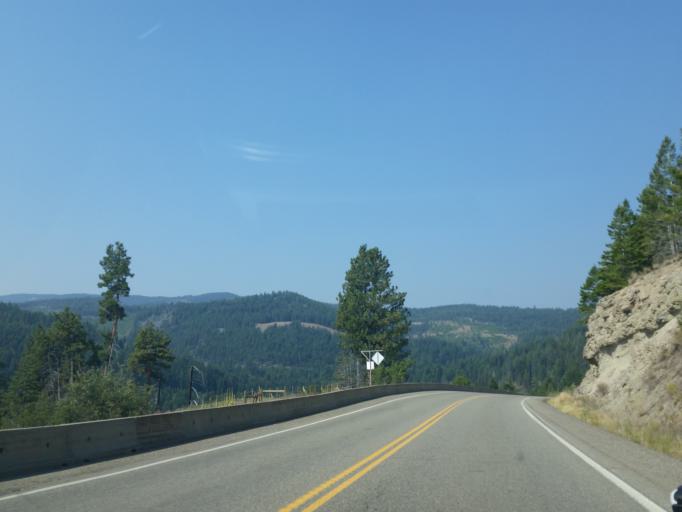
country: CA
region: British Columbia
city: Princeton
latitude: 49.3000
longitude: -120.5755
